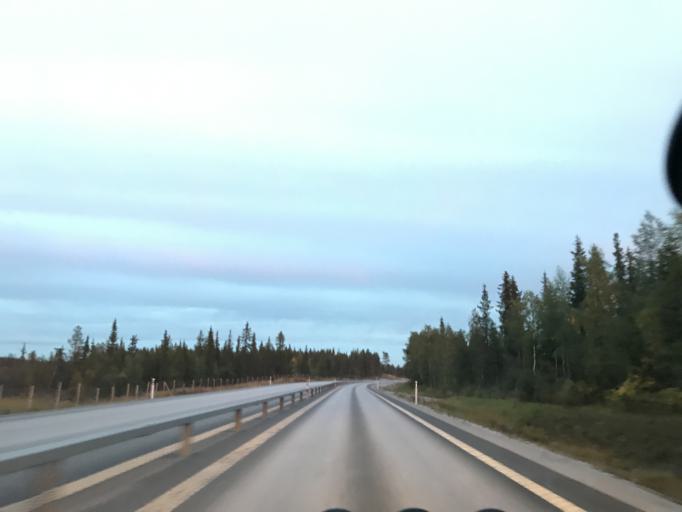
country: SE
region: Norrbotten
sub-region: Gallivare Kommun
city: Malmberget
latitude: 67.6597
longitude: 21.0015
